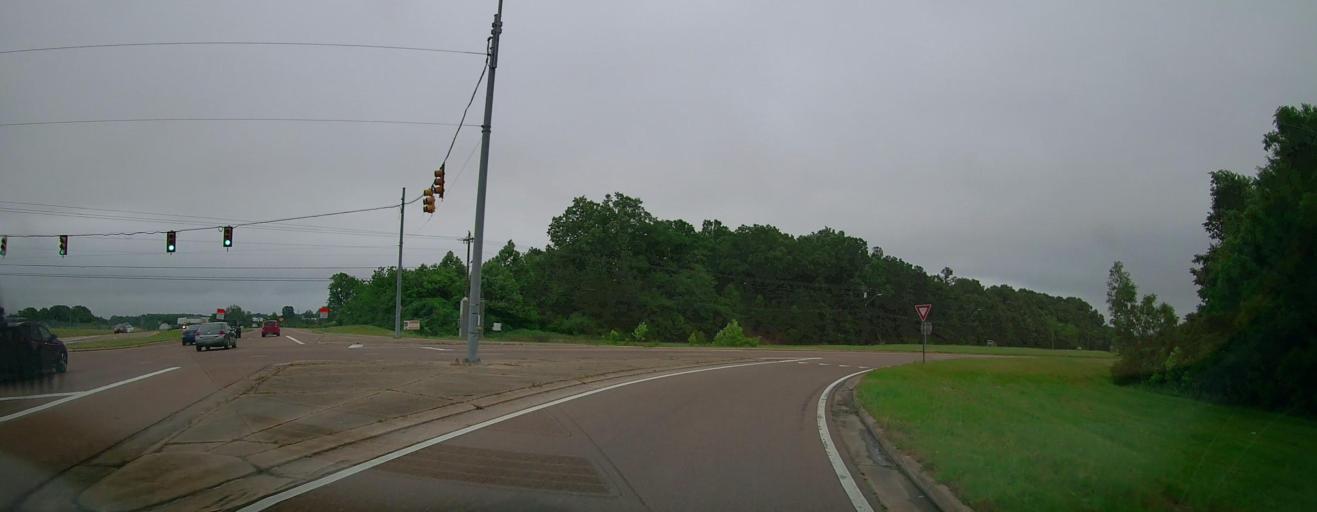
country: US
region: Mississippi
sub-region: De Soto County
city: Olive Branch
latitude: 34.9620
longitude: -89.7964
